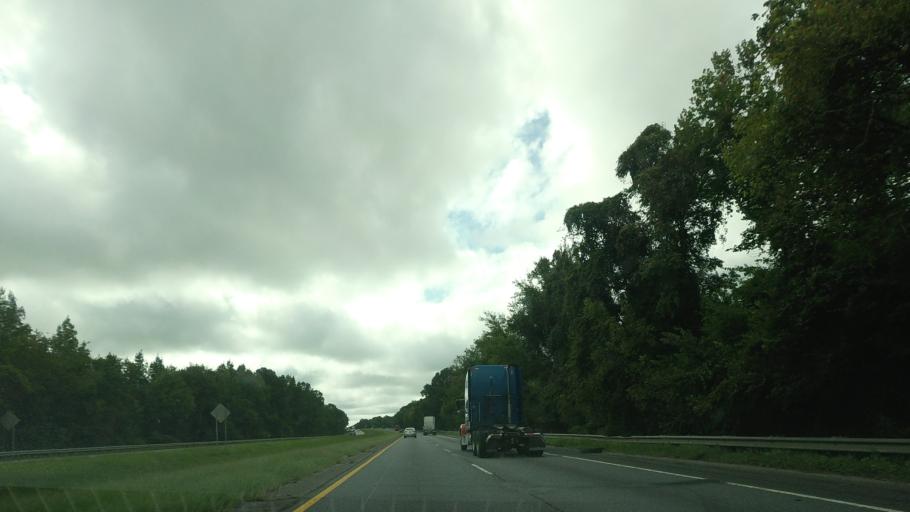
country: US
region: Georgia
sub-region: Bibb County
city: Macon
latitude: 32.8283
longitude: -83.6037
